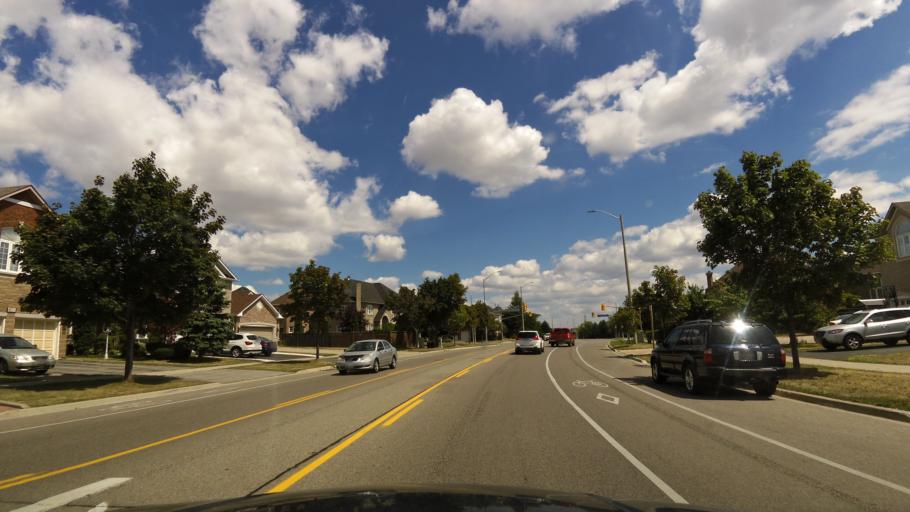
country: CA
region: Ontario
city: Mississauga
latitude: 43.6192
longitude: -79.6514
